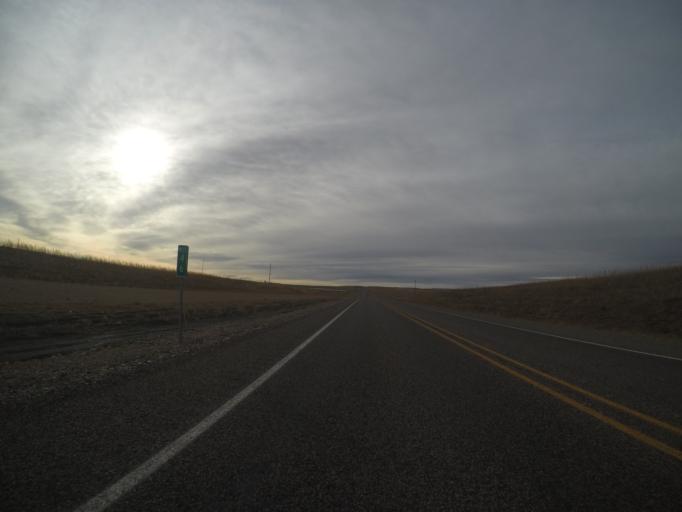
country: US
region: Montana
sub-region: Yellowstone County
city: Laurel
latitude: 45.5659
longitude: -108.8527
